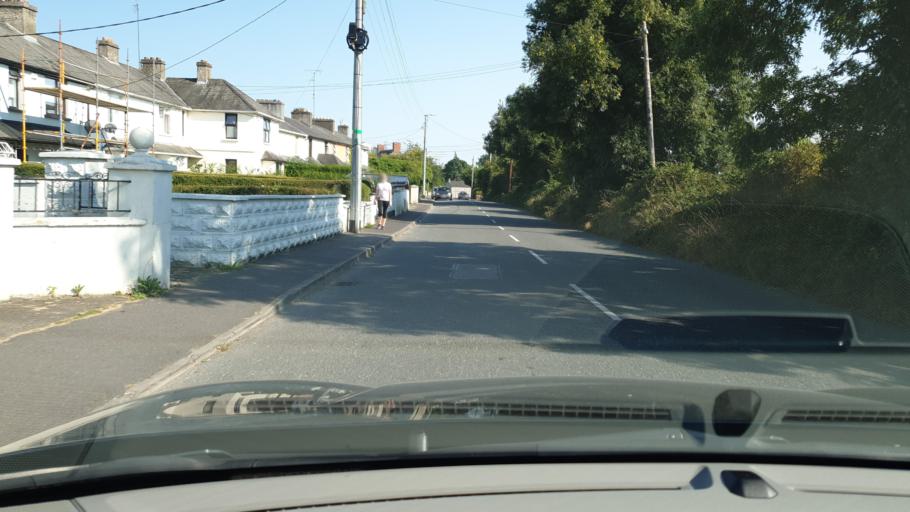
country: IE
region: Leinster
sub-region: An Mhi
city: Navan
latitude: 53.6577
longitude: -6.6841
